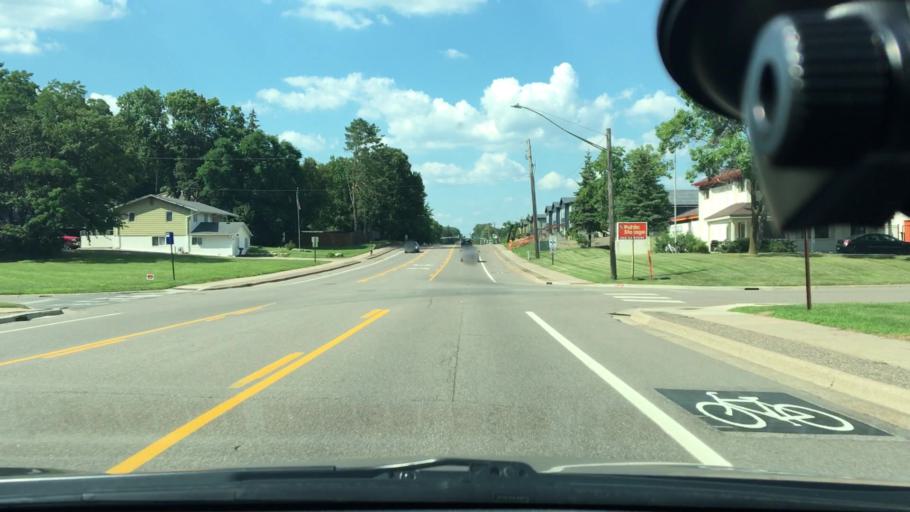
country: US
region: Minnesota
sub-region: Hennepin County
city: Golden Valley
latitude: 45.0035
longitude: -93.3803
